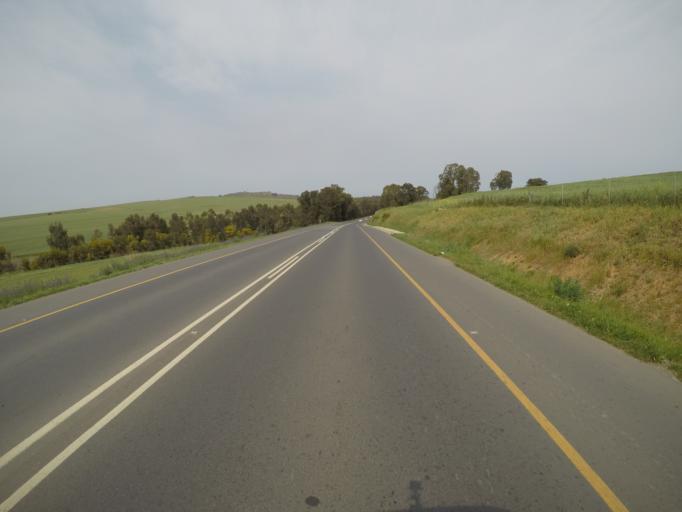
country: ZA
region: Western Cape
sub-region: West Coast District Municipality
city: Malmesbury
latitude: -33.4561
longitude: 18.7477
